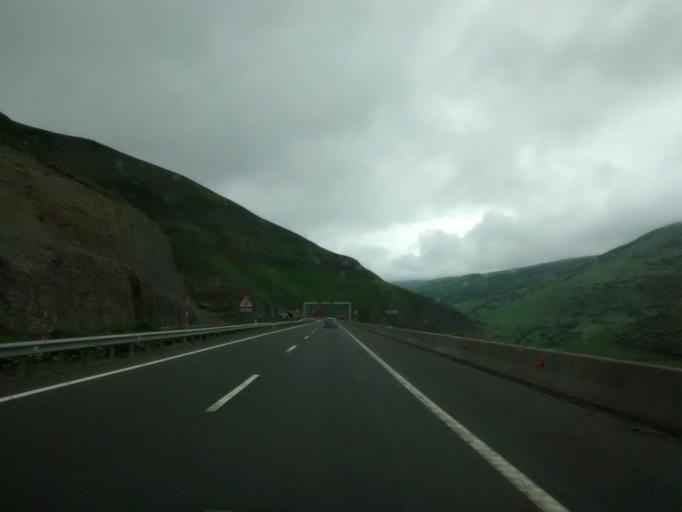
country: ES
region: Cantabria
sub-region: Provincia de Cantabria
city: Santiurde de Reinosa
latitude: 43.0405
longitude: -4.0898
